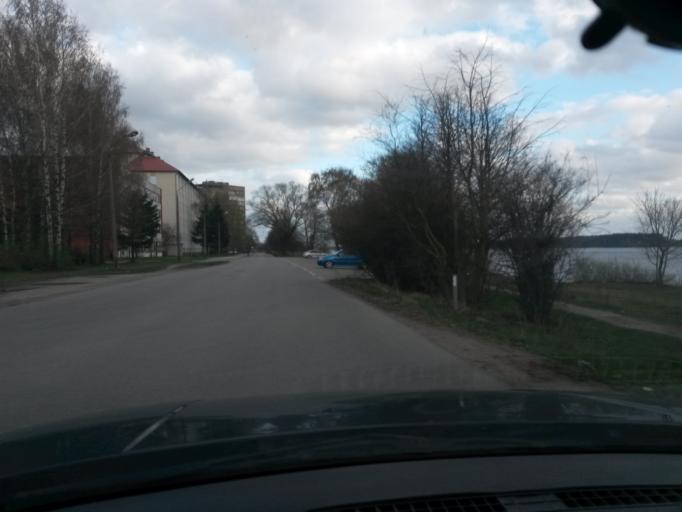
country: LV
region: Kekava
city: Balozi
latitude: 56.9170
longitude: 24.1634
